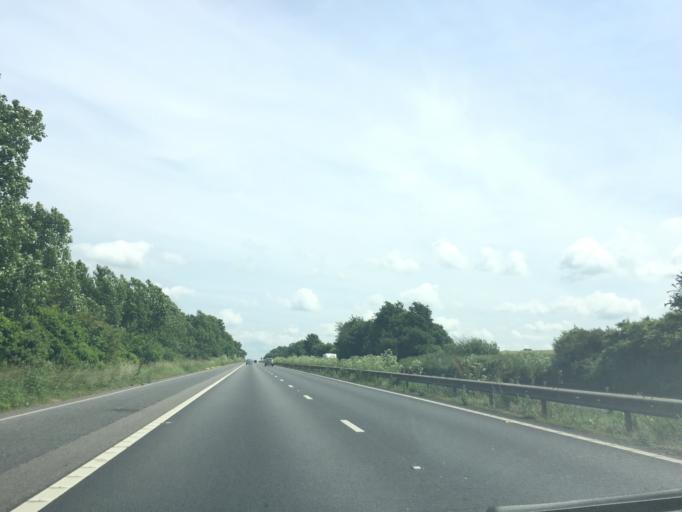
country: GB
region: England
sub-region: Kent
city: Newington
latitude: 51.3359
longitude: 0.6467
